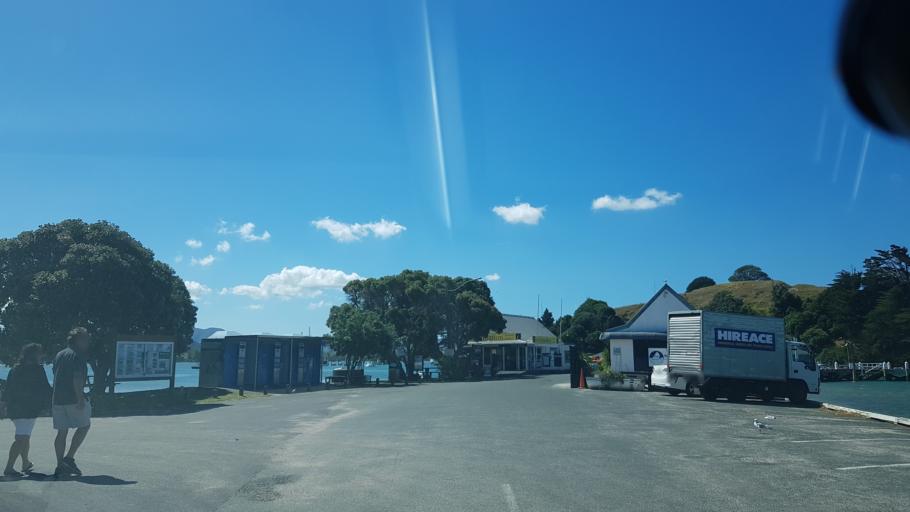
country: NZ
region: Auckland
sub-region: Auckland
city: Warkworth
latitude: -36.3898
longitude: 174.7292
